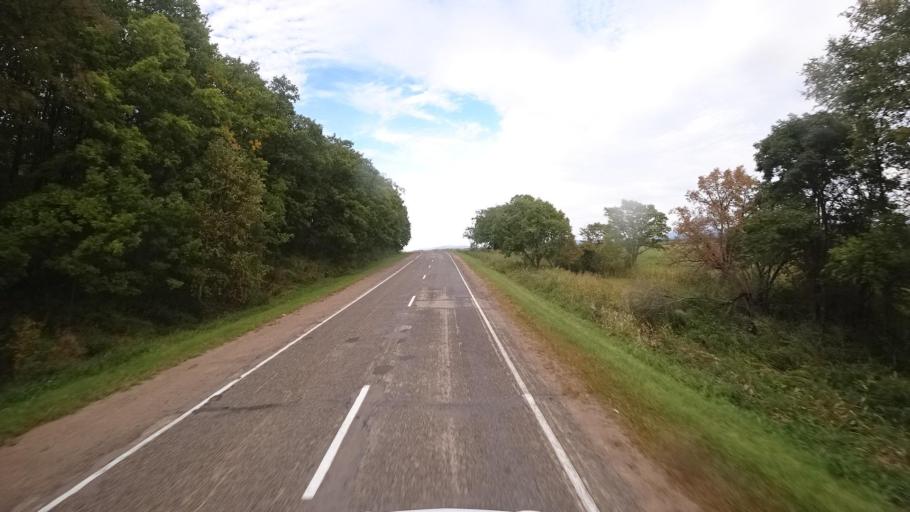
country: RU
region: Primorskiy
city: Dostoyevka
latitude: 44.3545
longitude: 133.4249
